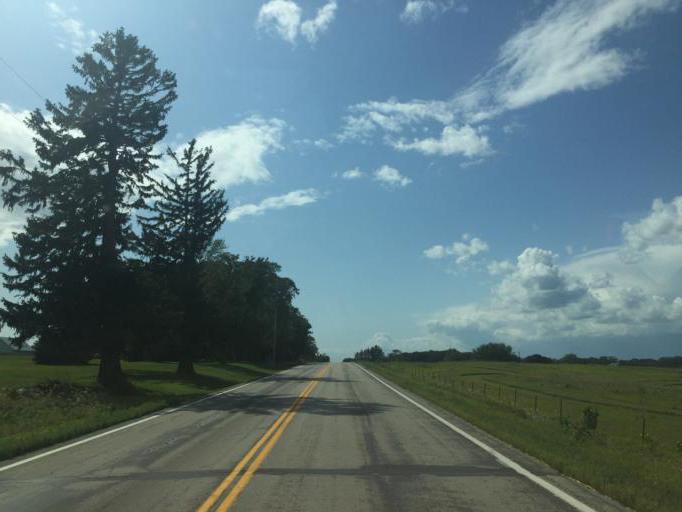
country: US
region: Minnesota
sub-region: Olmsted County
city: Rochester
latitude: 43.9640
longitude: -92.5226
